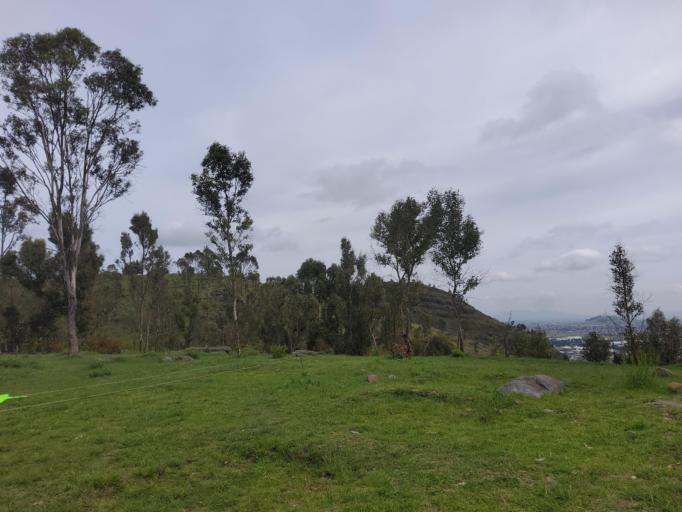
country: MX
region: Mexico
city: Toluca
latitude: 19.3032
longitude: -99.6584
